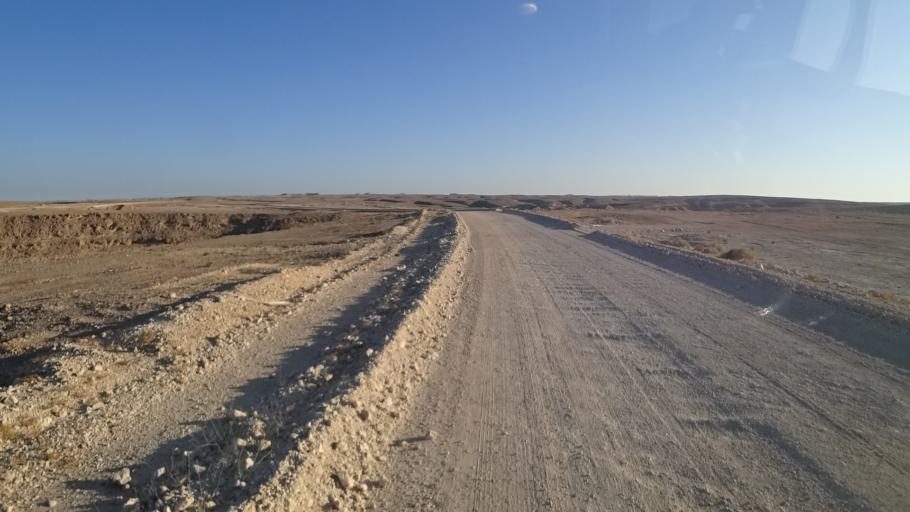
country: YE
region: Al Mahrah
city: Hawf
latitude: 17.1895
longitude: 53.3385
